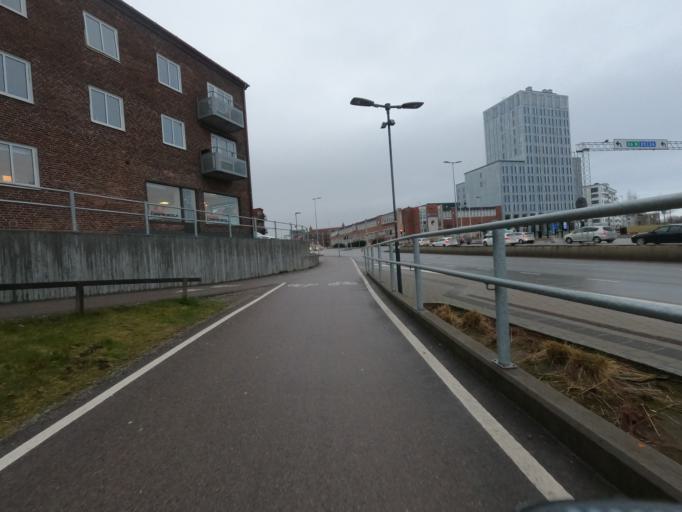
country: SE
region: Halland
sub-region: Halmstads Kommun
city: Halmstad
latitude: 56.6713
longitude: 12.8668
